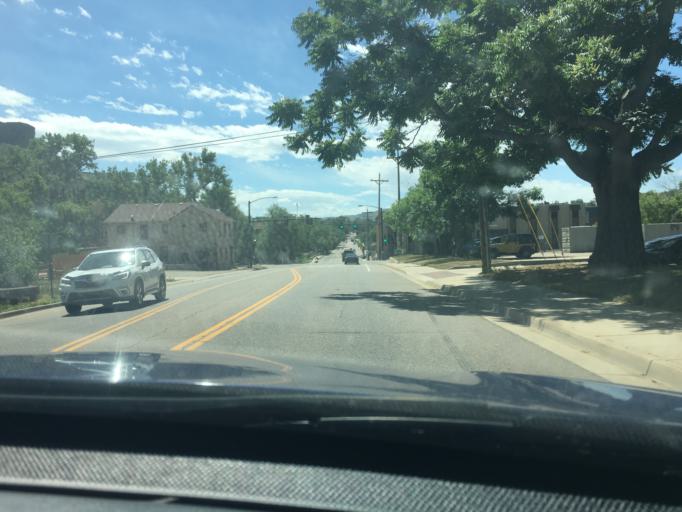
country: US
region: Colorado
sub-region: Jefferson County
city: Golden
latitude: 39.7593
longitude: -105.2219
